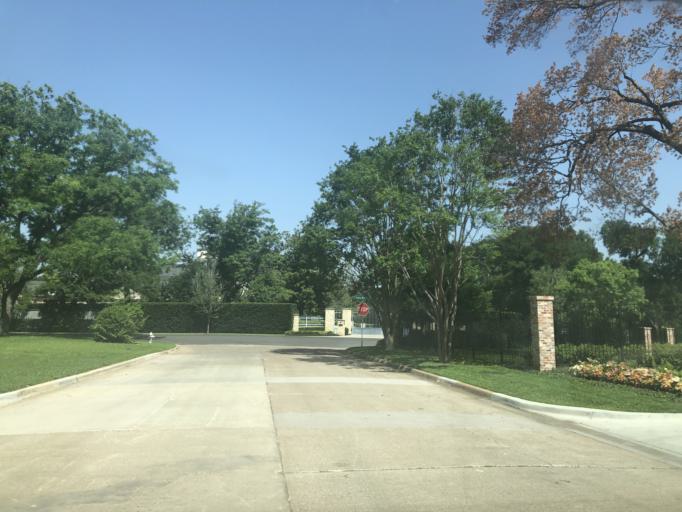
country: US
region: Texas
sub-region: Dallas County
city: University Park
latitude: 32.8718
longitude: -96.8240
